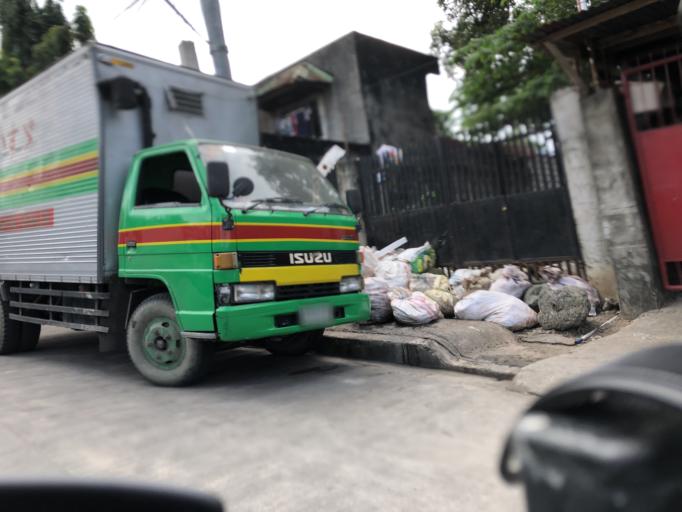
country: PH
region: Central Luzon
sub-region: Province of Bulacan
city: San Jose del Monte
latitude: 14.7520
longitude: 121.0572
